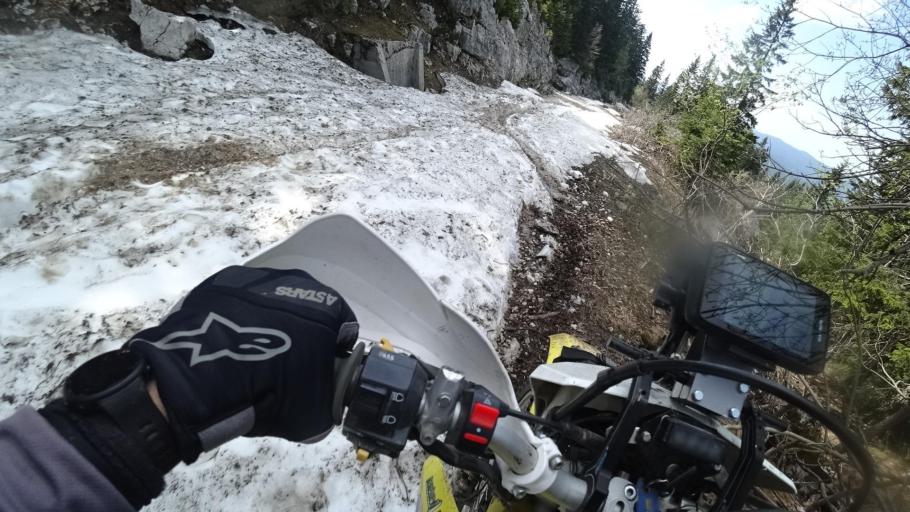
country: BA
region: Republika Srpska
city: Sipovo
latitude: 44.1264
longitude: 17.0487
